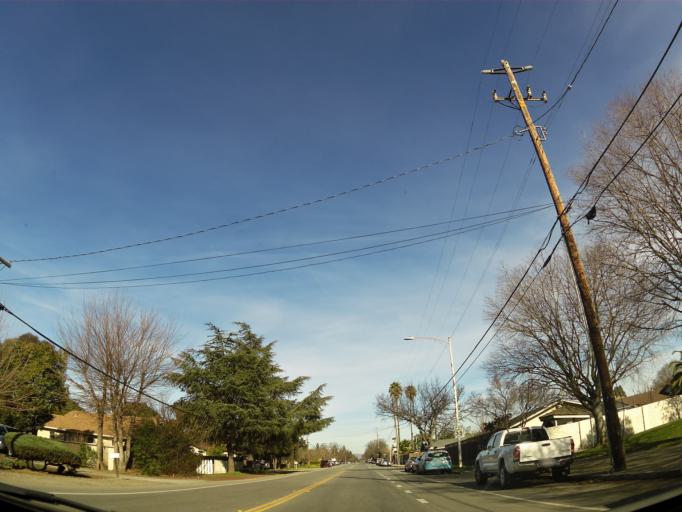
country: US
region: California
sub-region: Santa Clara County
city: Gilroy
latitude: 37.0225
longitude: -121.5698
